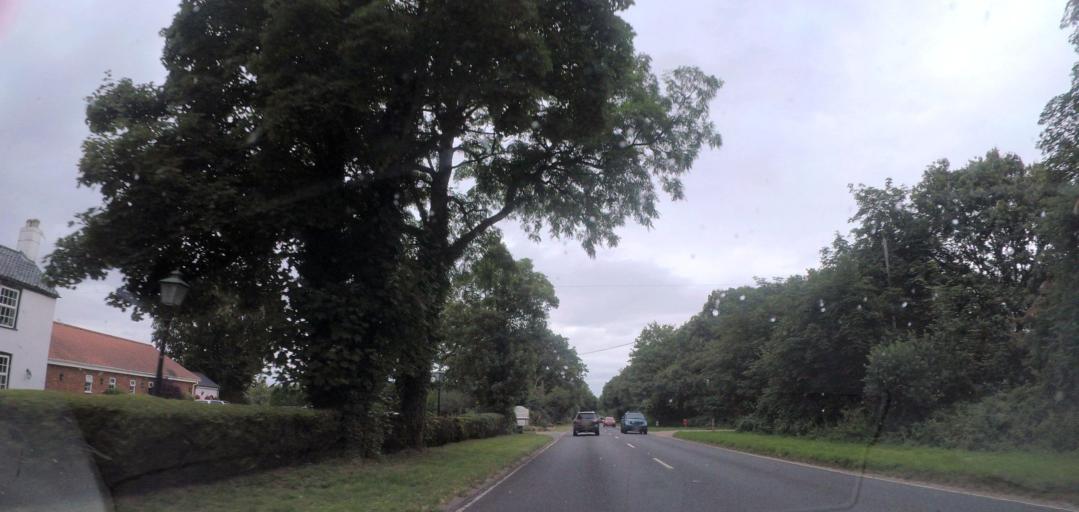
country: GB
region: England
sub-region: Norfolk
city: Spixworth
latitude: 52.6936
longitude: 1.3374
